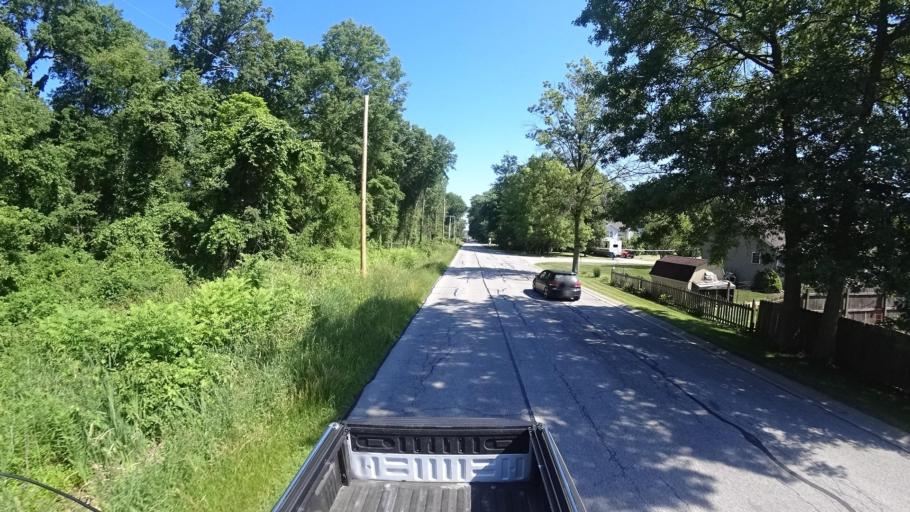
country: US
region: Indiana
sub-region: Porter County
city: Porter
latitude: 41.5961
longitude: -87.1053
